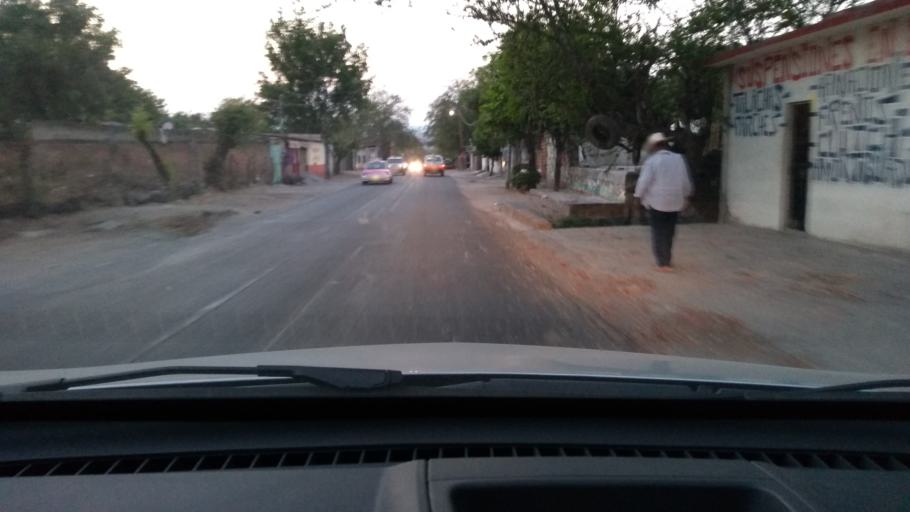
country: MX
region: Morelos
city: Coatetelco
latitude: 18.7266
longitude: -99.3177
